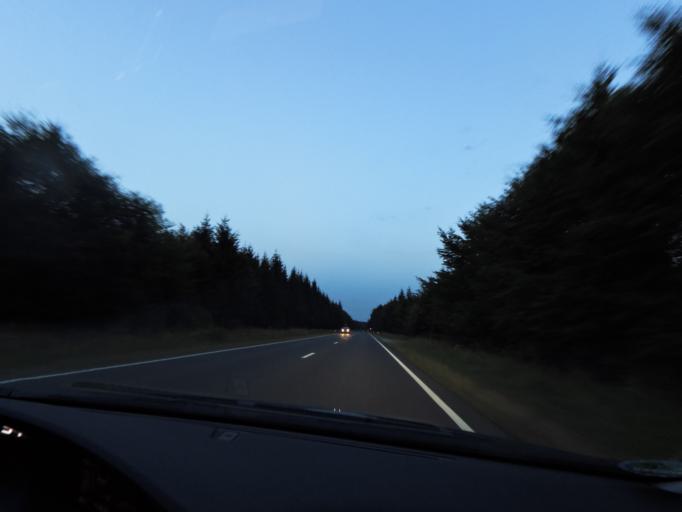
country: BE
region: Wallonia
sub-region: Province de Liege
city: Malmedy
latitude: 50.5137
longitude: 6.0720
